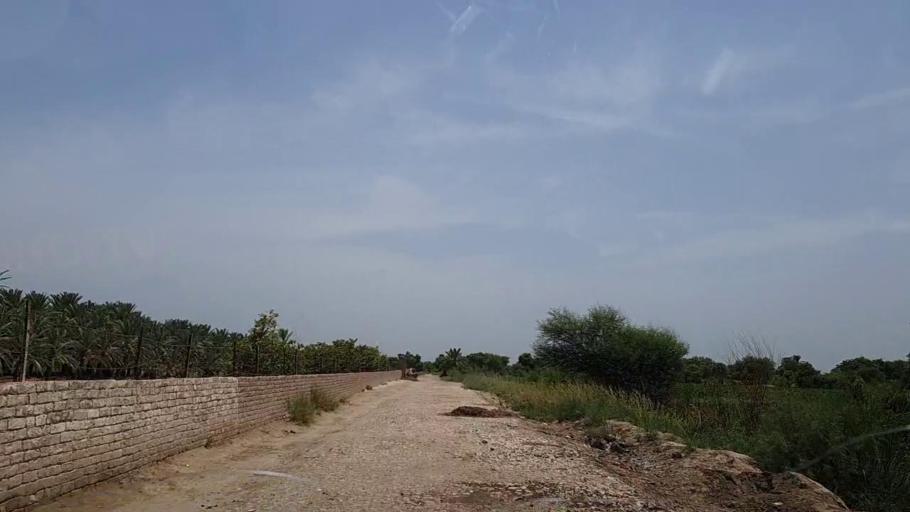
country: PK
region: Sindh
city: Khanpur
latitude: 27.7866
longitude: 69.4946
